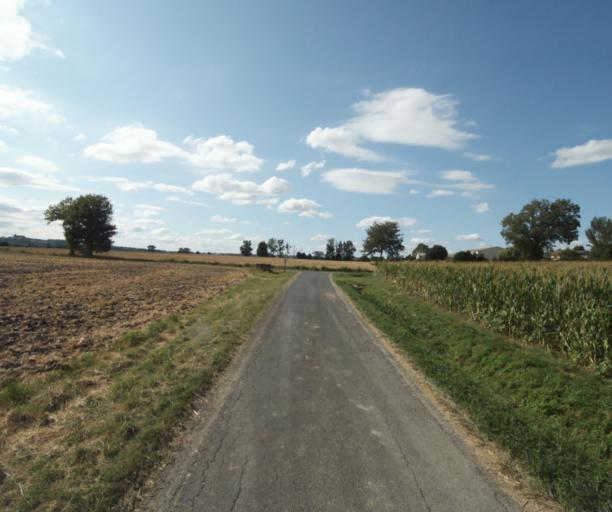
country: FR
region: Midi-Pyrenees
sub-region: Departement du Tarn
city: Puylaurens
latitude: 43.5240
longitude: 1.9780
